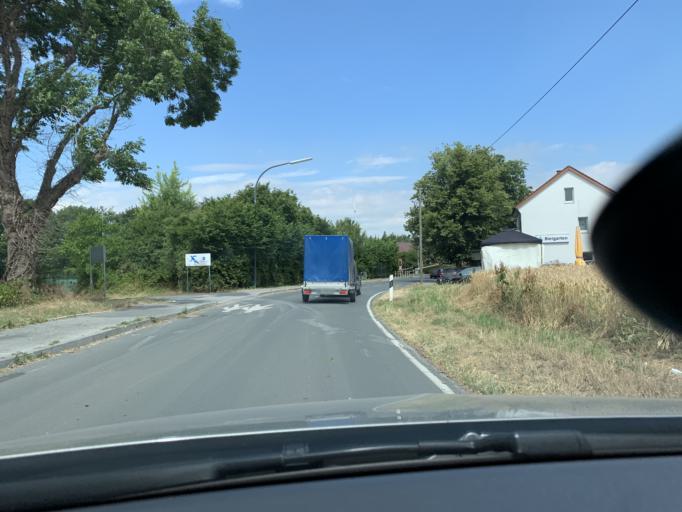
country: DE
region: North Rhine-Westphalia
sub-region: Regierungsbezirk Arnsberg
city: Lippstadt
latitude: 51.6716
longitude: 8.3984
